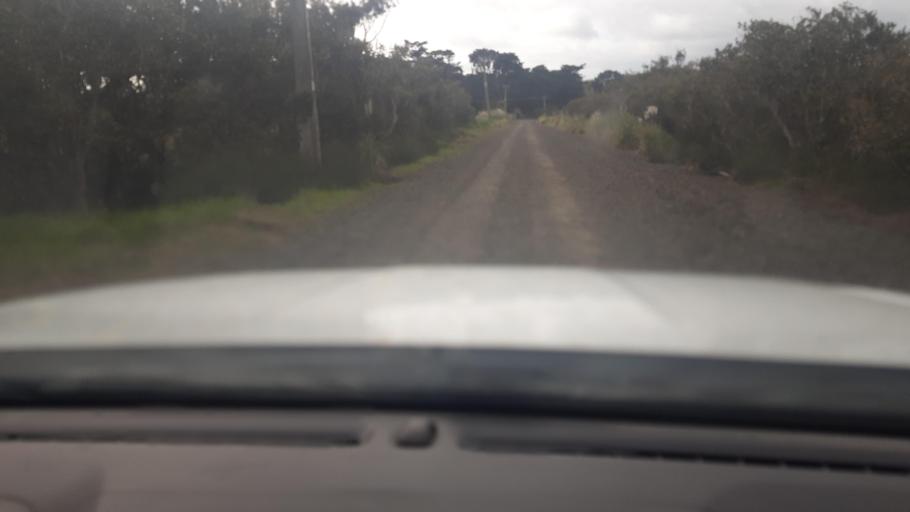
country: NZ
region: Northland
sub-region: Far North District
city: Ahipara
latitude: -35.2587
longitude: 173.2080
